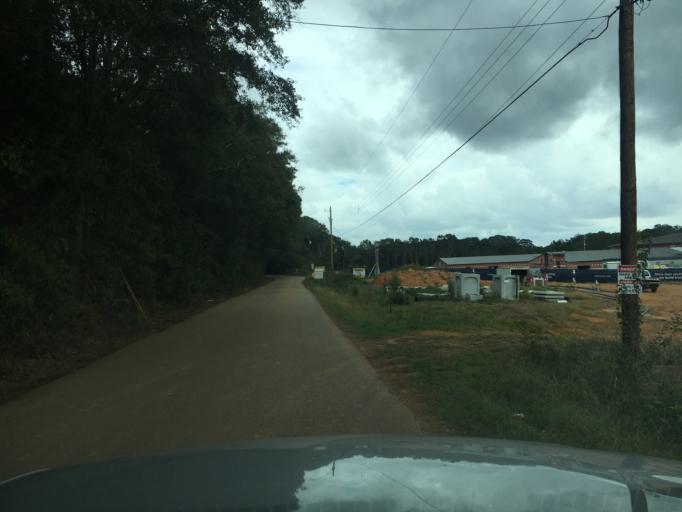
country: US
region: South Carolina
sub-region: Spartanburg County
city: Duncan
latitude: 34.8618
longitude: -82.1095
